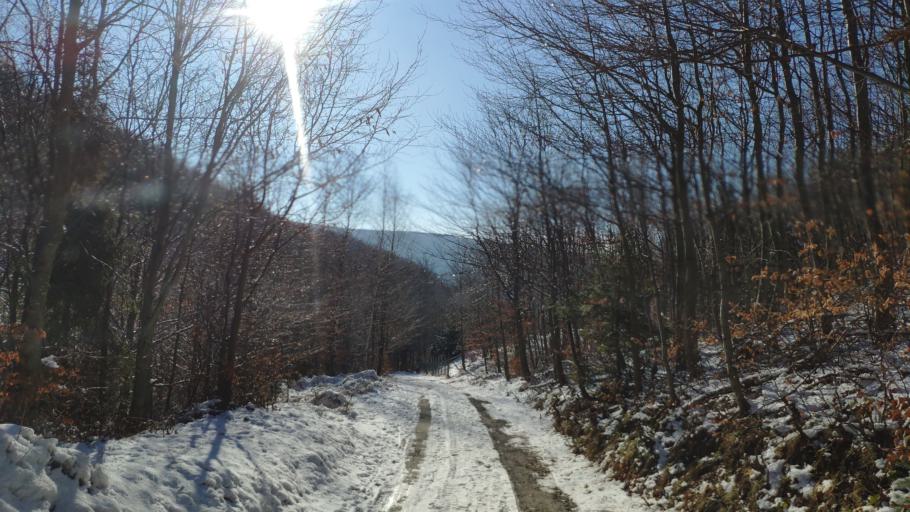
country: SK
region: Kosicky
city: Gelnica
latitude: 48.7591
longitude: 21.0076
